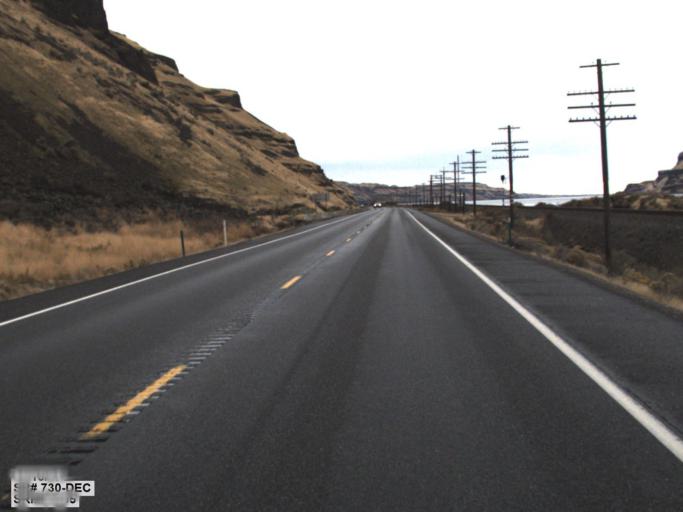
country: US
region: Washington
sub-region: Benton County
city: Finley
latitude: 46.0044
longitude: -118.9710
